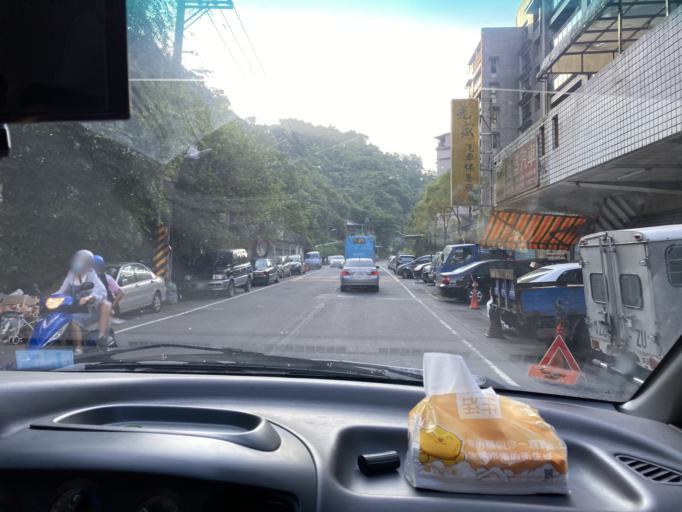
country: TW
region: Taiwan
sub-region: Keelung
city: Keelung
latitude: 25.0988
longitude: 121.7377
